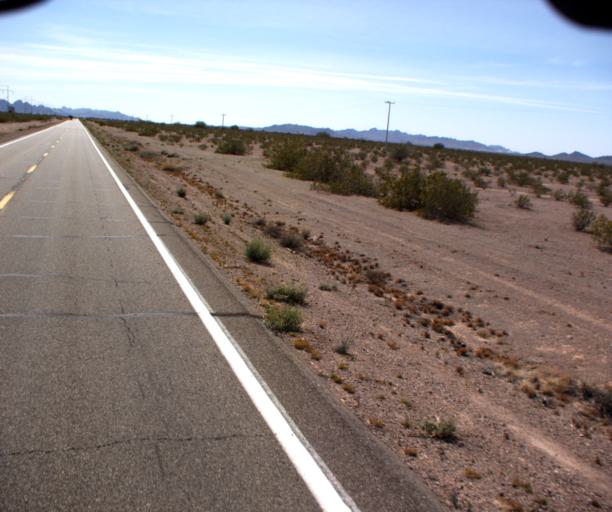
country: US
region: Arizona
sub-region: La Paz County
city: Quartzsite
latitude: 33.4216
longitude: -114.2170
